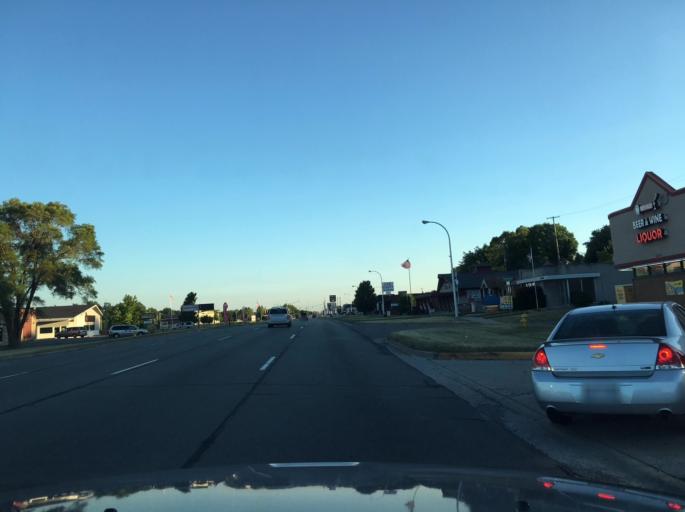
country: US
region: Michigan
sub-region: Macomb County
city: Mount Clemens
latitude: 42.5805
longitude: -82.8861
